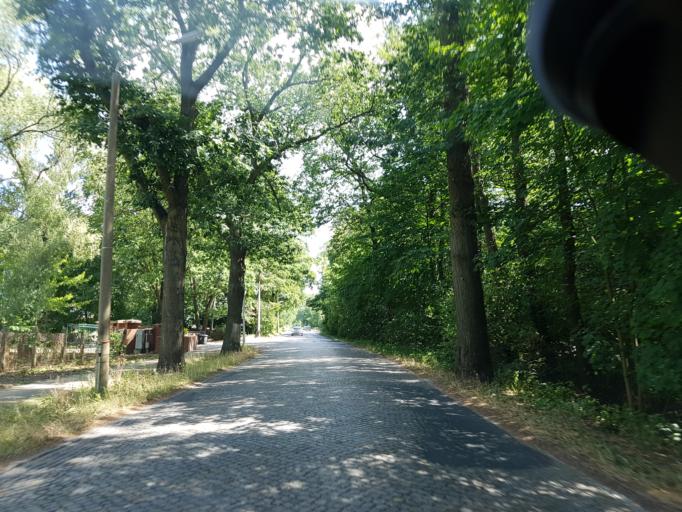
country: DE
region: Brandenburg
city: Cottbus
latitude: 51.7202
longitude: 14.3540
